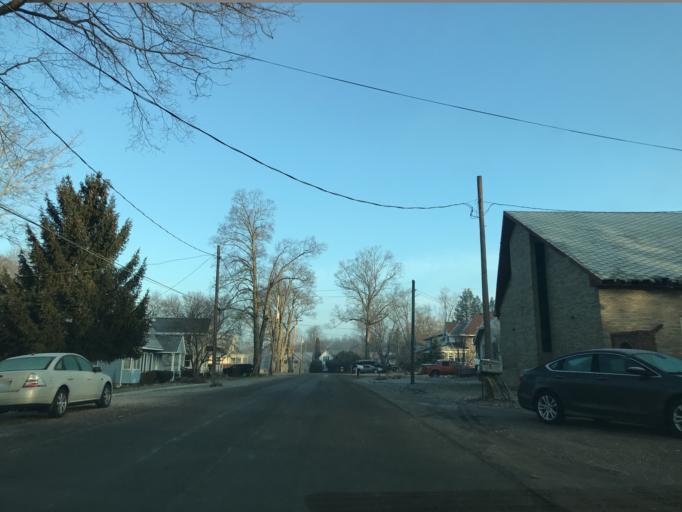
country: US
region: Michigan
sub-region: Ingham County
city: Leslie
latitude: 42.3843
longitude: -84.4610
